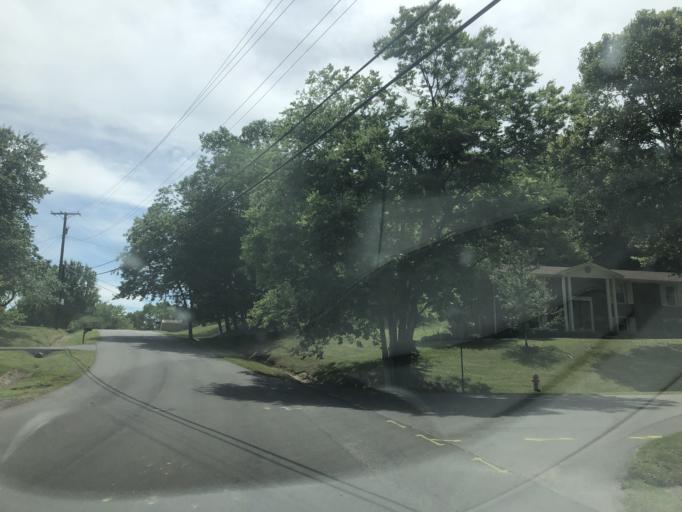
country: US
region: Tennessee
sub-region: Davidson County
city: Belle Meade
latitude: 36.0764
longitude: -86.9319
